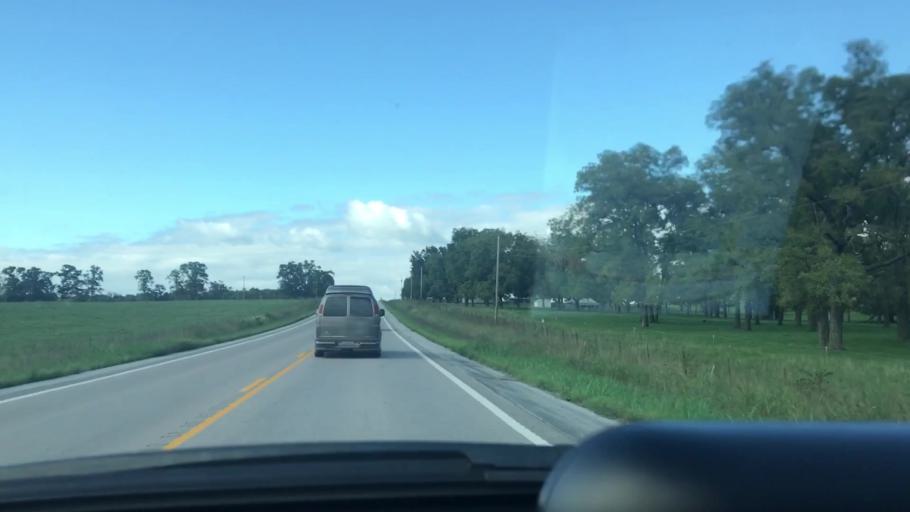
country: US
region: Missouri
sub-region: Hickory County
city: Hermitage
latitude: 37.9710
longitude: -93.2063
